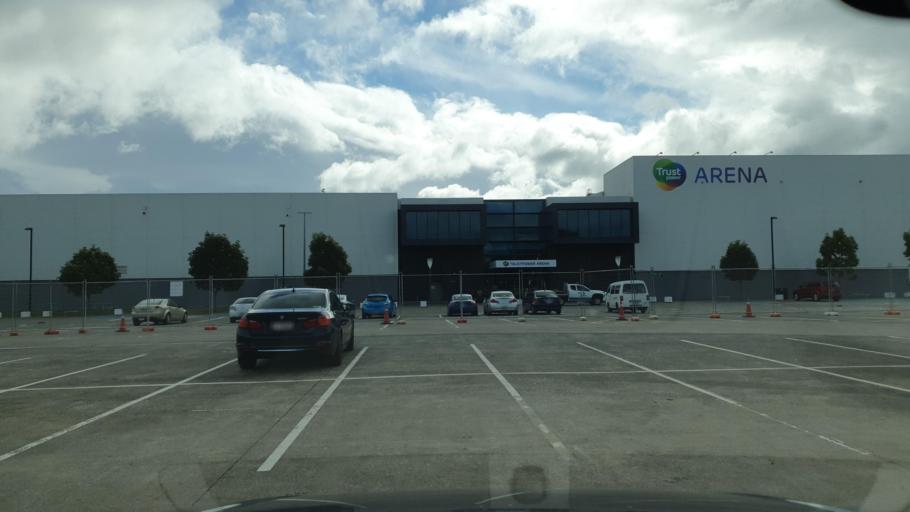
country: NZ
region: Bay of Plenty
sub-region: Tauranga City
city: Tauranga
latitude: -37.6865
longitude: 176.2251
